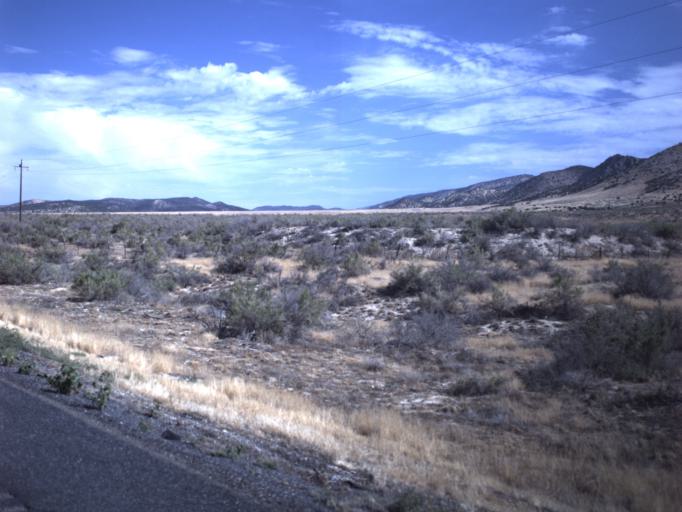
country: US
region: Utah
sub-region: Sanpete County
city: Gunnison
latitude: 39.2940
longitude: -111.8889
